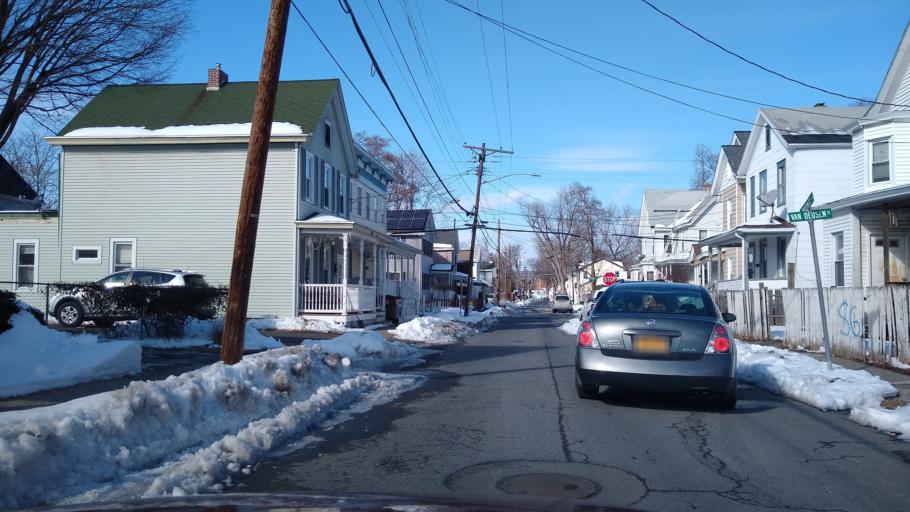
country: US
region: New York
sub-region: Ulster County
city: Kingston
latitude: 41.9287
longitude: -74.0092
